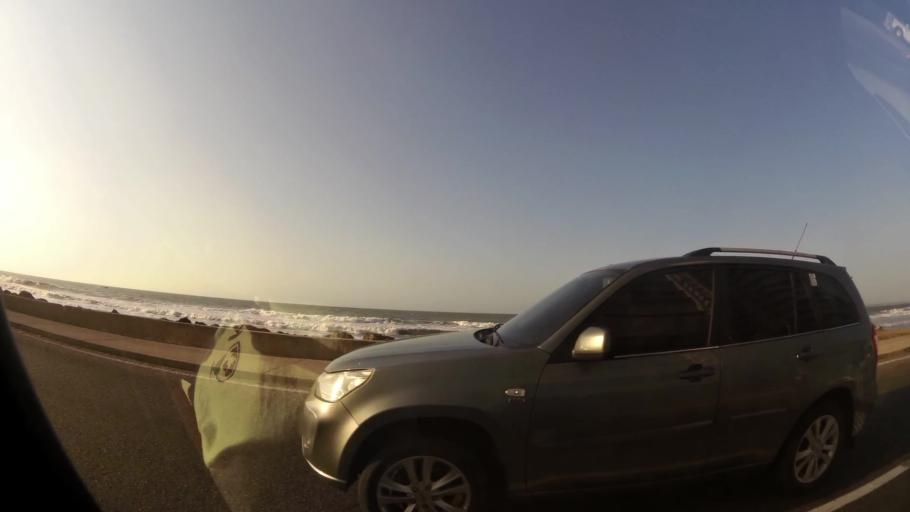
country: CO
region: Bolivar
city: Cartagena
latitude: 10.4369
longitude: -75.5358
